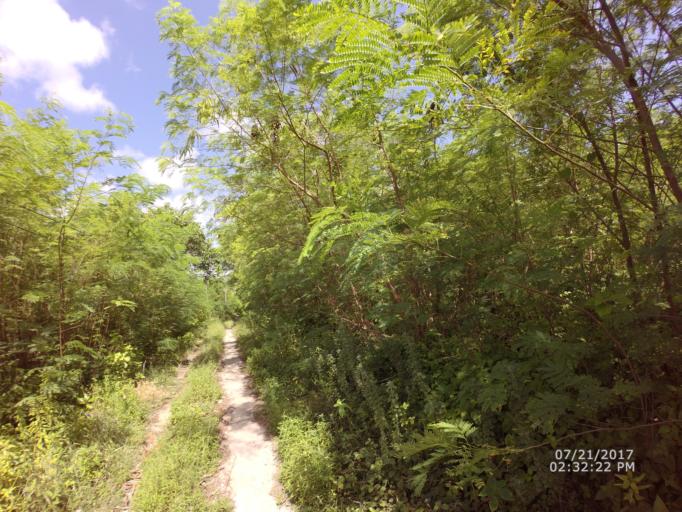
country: TH
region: Phangnga
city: Ban Phru Nai
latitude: 7.7616
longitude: 98.7659
